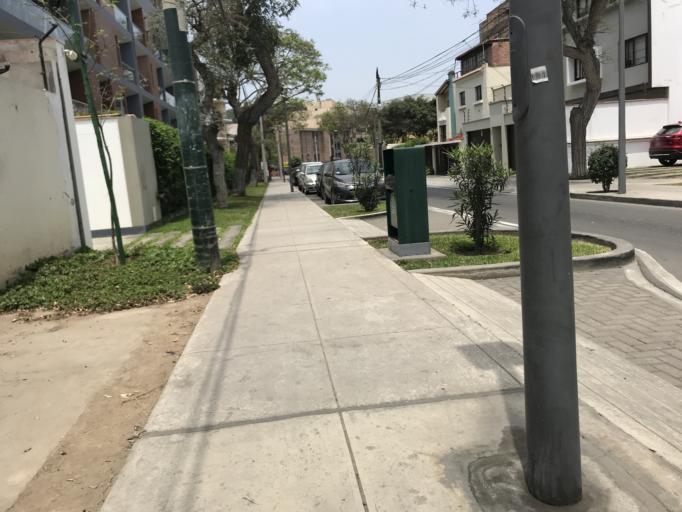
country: PE
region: Lima
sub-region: Lima
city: San Isidro
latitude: -12.0898
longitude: -77.0494
